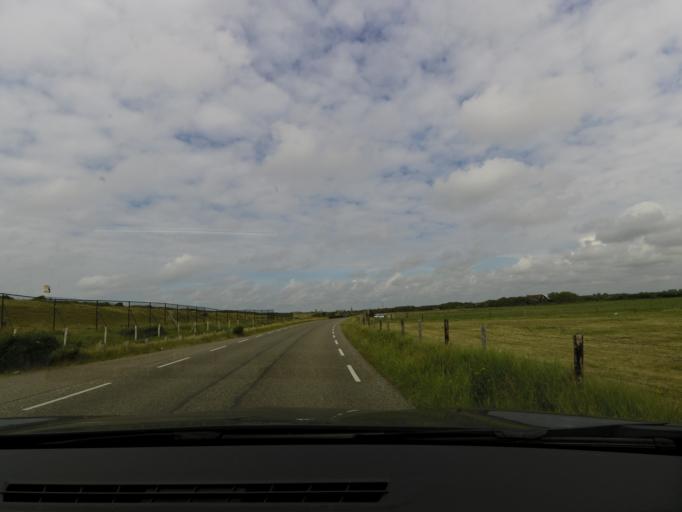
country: NL
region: Zeeland
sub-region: Gemeente Middelburg
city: Middelburg
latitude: 51.5555
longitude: 3.4750
